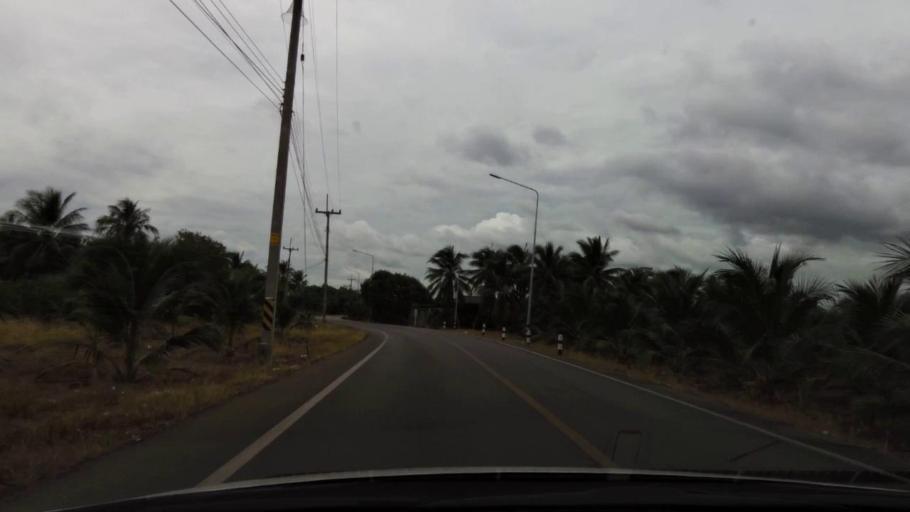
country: TH
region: Ratchaburi
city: Damnoen Saduak
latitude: 13.5669
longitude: 100.0111
